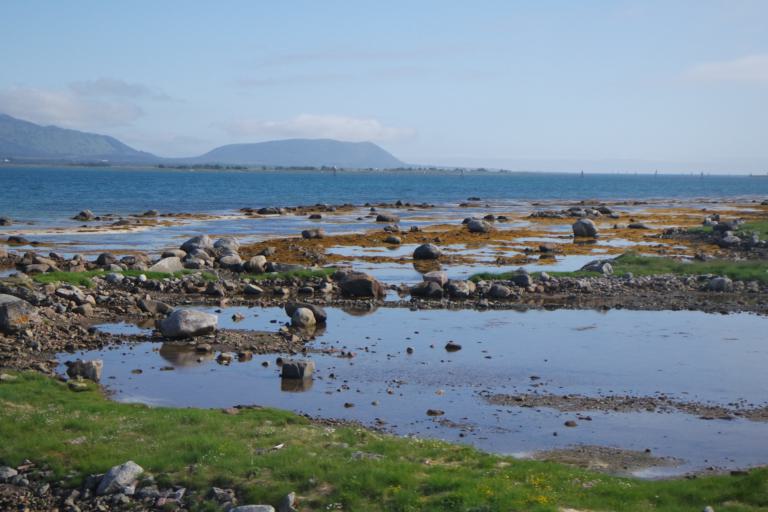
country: NO
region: Nordland
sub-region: Andoy
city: Myre
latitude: 68.9639
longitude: 15.6412
